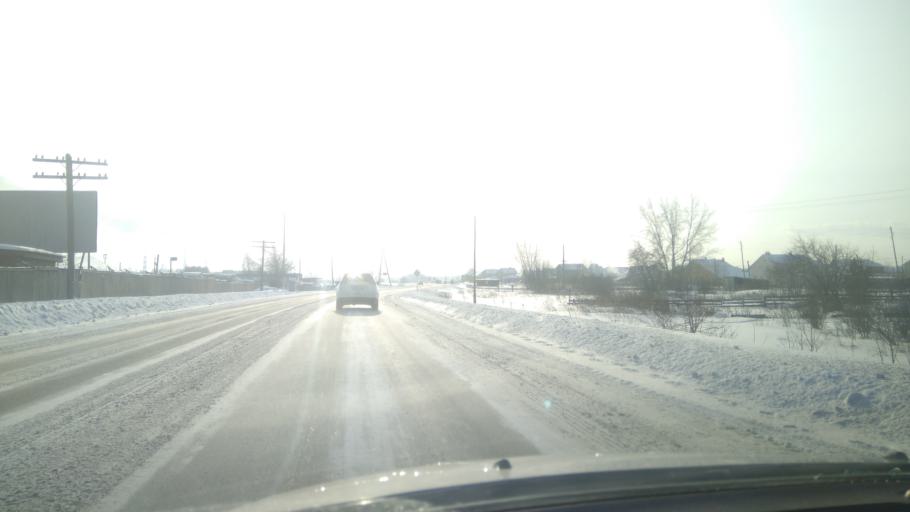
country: RU
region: Sverdlovsk
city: Sukhoy Log
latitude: 56.8887
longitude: 62.0423
